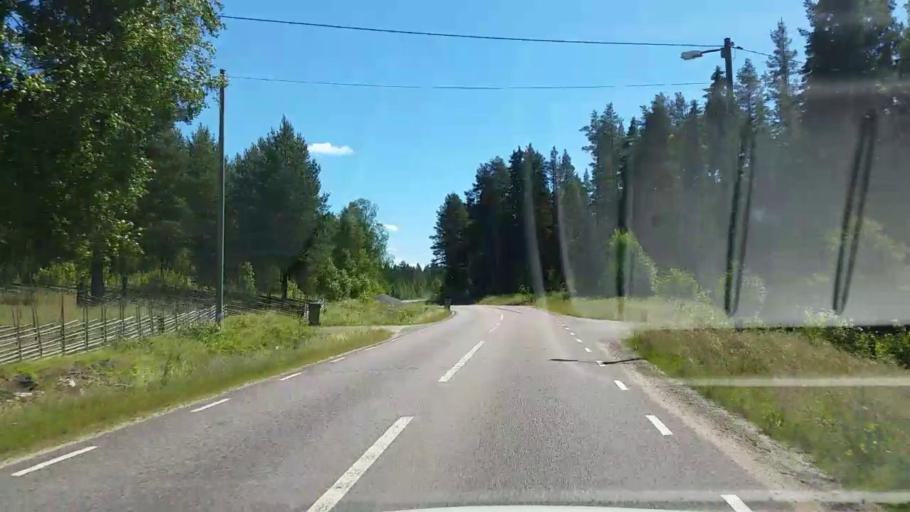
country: SE
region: Gaevleborg
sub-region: Ovanakers Kommun
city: Edsbyn
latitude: 61.4529
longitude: 15.7074
